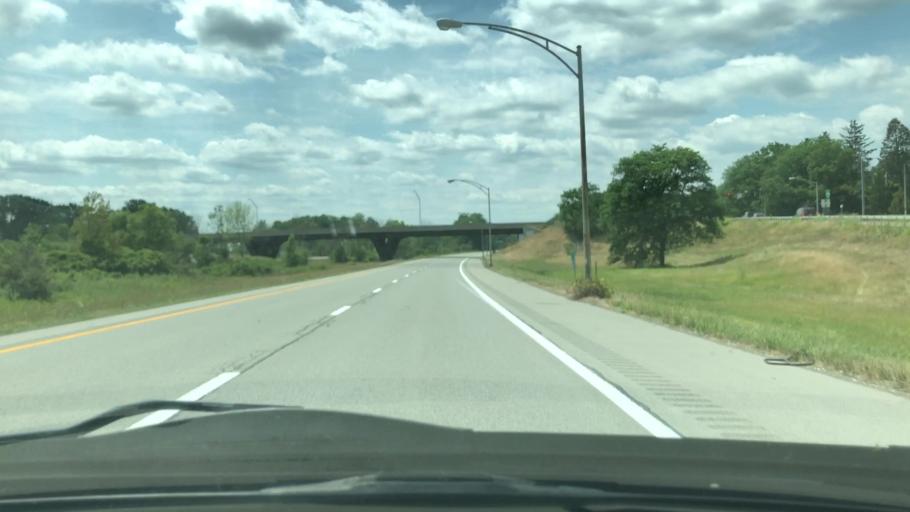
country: US
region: New York
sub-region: Monroe County
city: Churchville
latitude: 43.0969
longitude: -77.7970
